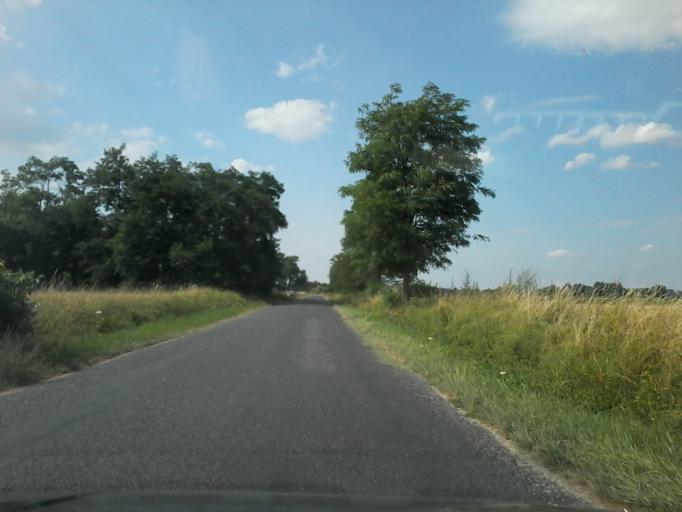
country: HU
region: Vas
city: Celldomolk
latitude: 47.2109
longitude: 17.0928
